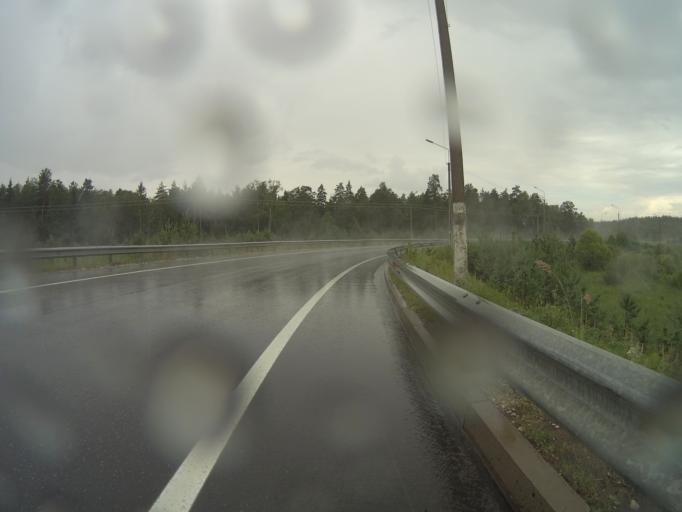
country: RU
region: Vladimir
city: Kommunar
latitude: 56.0784
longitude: 40.4709
